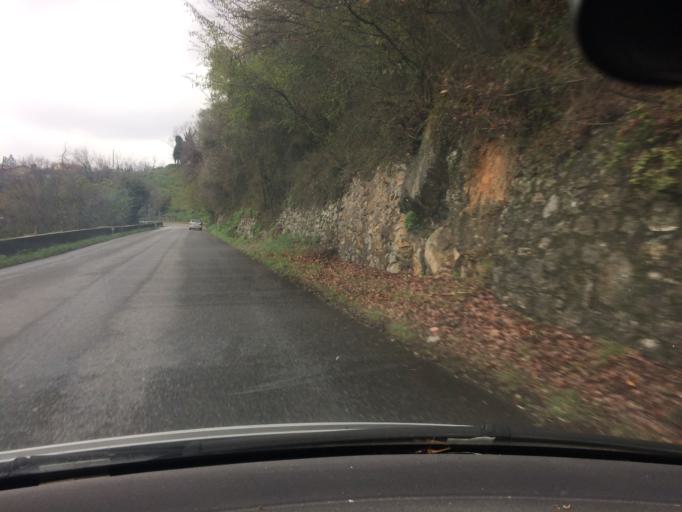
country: IT
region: Tuscany
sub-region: Provincia di Massa-Carrara
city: Massa
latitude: 44.0648
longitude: 10.1147
